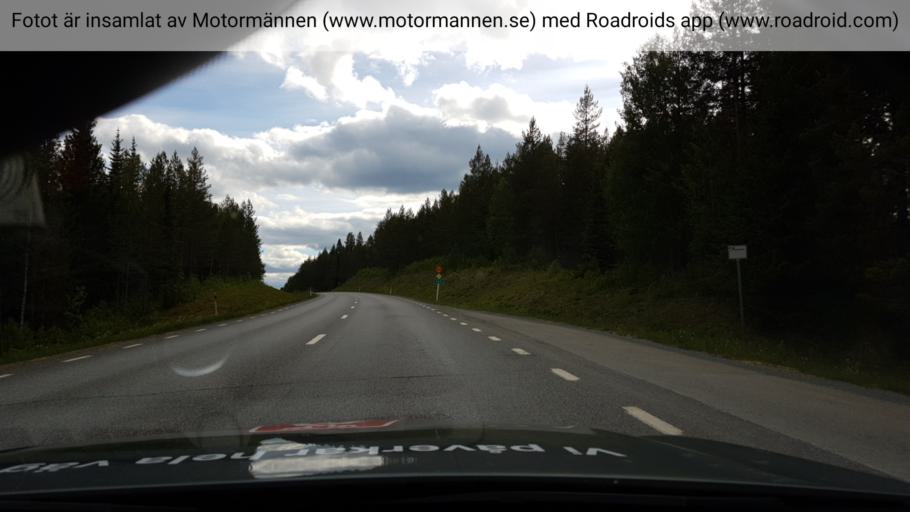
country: SE
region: Jaemtland
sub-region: OEstersunds Kommun
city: Lit
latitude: 63.3968
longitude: 14.9767
